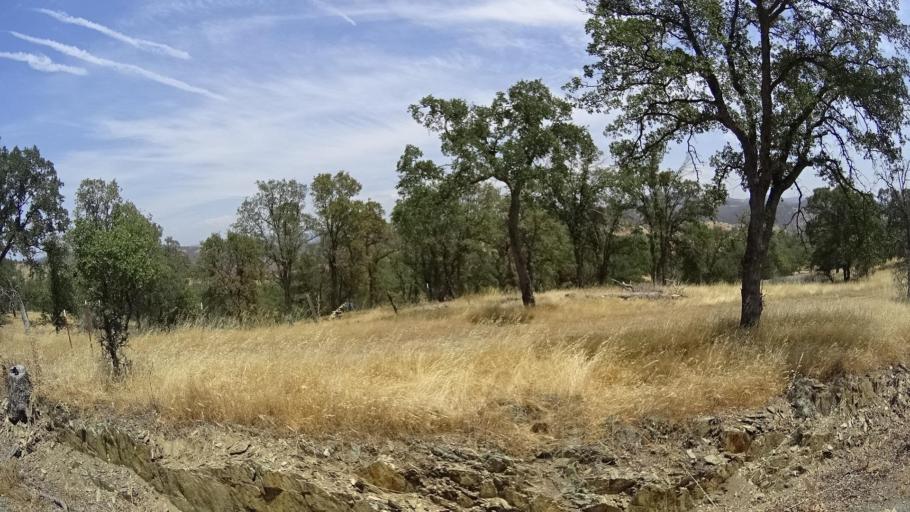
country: US
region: California
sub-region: Tuolumne County
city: Tuolumne City
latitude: 37.6440
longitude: -120.2996
